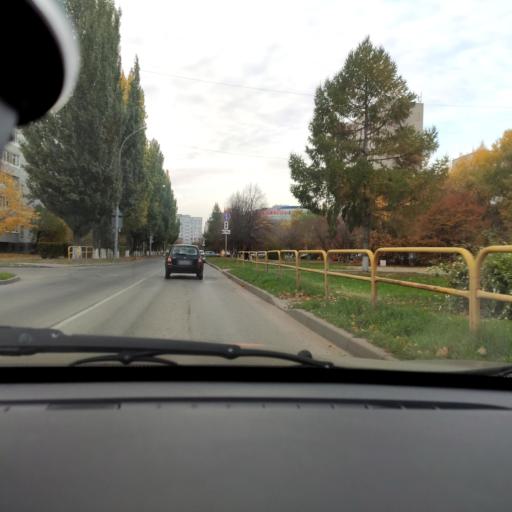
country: RU
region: Samara
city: Tol'yatti
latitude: 53.5363
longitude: 49.3211
